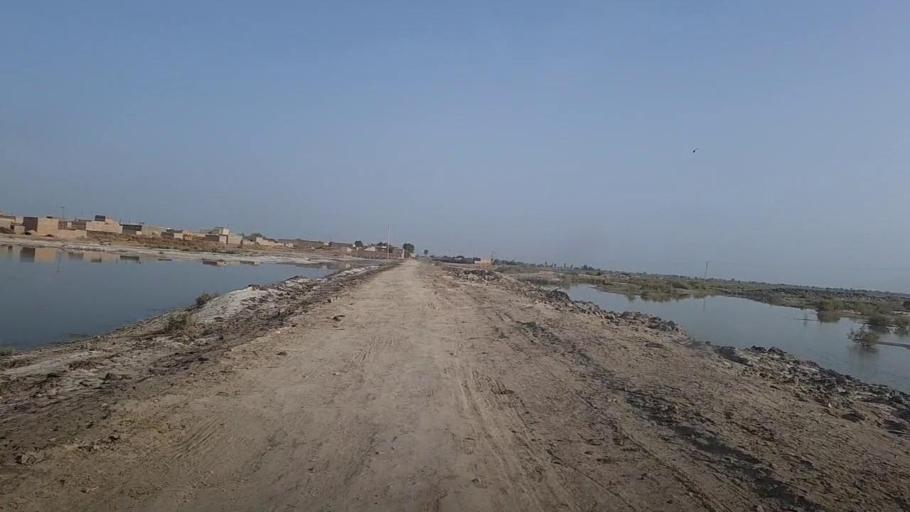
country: PK
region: Sindh
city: Sita Road
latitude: 27.1126
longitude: 67.8823
